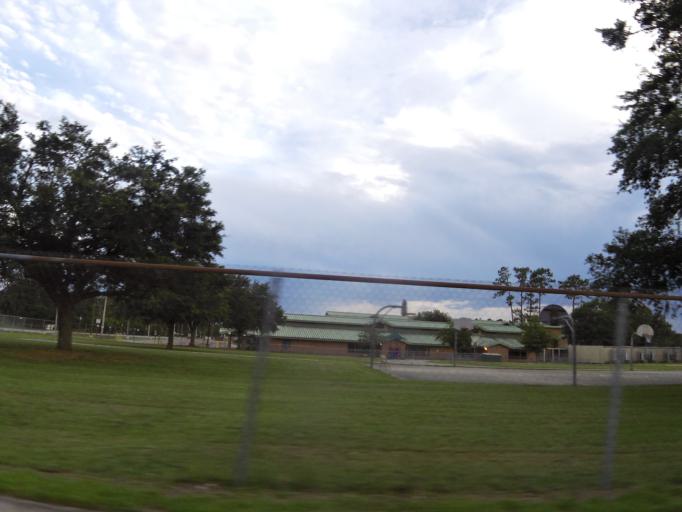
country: US
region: Florida
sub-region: Clay County
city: Bellair-Meadowbrook Terrace
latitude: 30.3021
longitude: -81.7987
